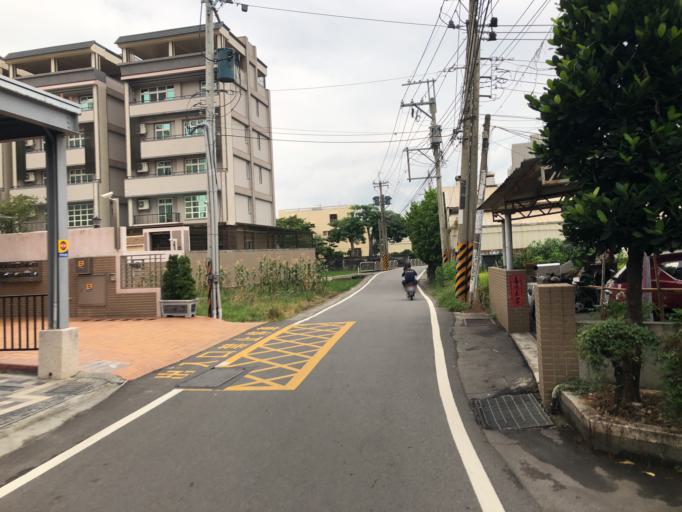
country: TW
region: Taiwan
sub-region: Taichung City
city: Taichung
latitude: 24.0626
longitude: 120.6818
